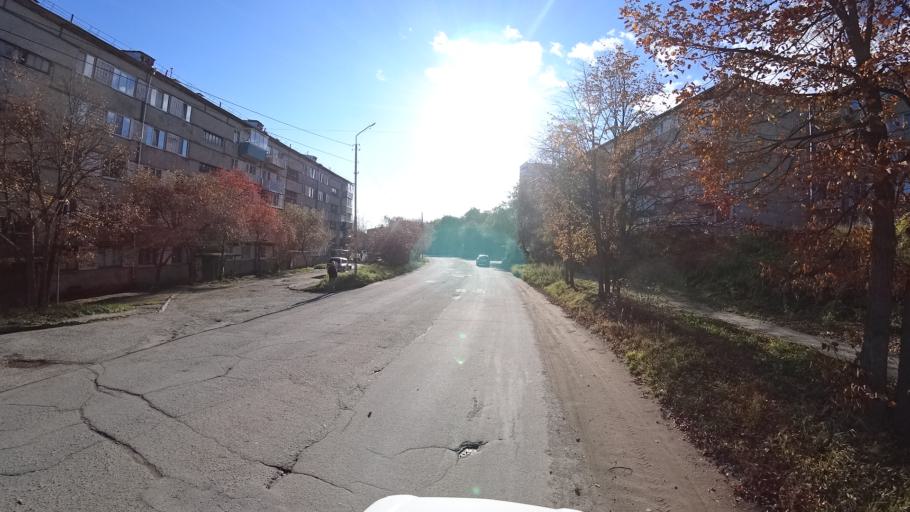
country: RU
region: Khabarovsk Krai
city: Amursk
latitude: 50.2422
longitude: 136.9064
